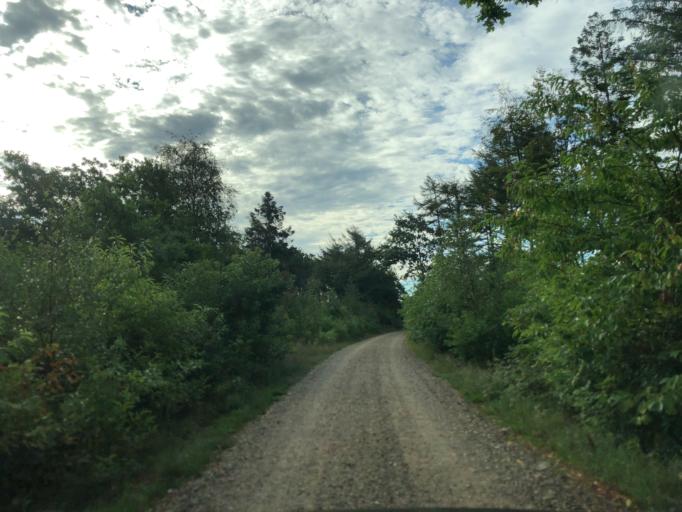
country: DK
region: Central Jutland
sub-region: Holstebro Kommune
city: Ulfborg
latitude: 56.1848
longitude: 8.3464
